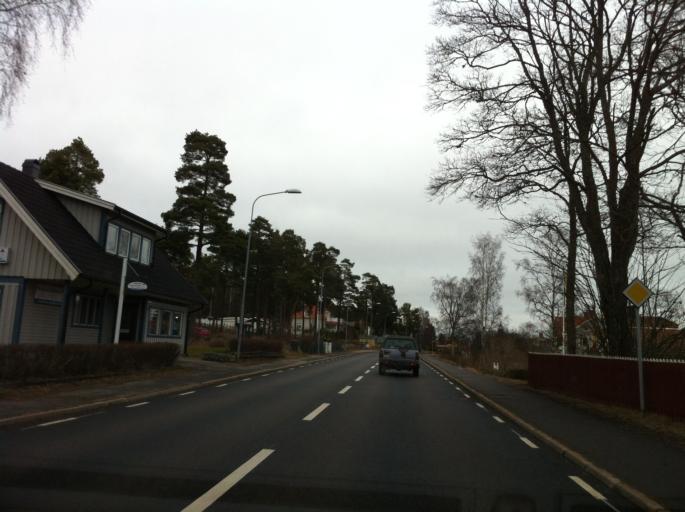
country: SE
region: Kalmar
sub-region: Vasterviks Kommun
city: Overum
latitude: 57.9081
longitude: 16.2428
